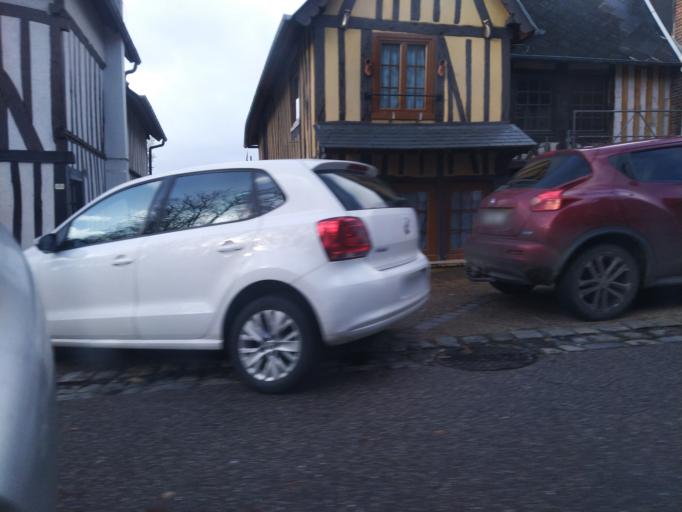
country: FR
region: Haute-Normandie
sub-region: Departement de la Seine-Maritime
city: Jumieges
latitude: 49.4334
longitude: 0.8201
